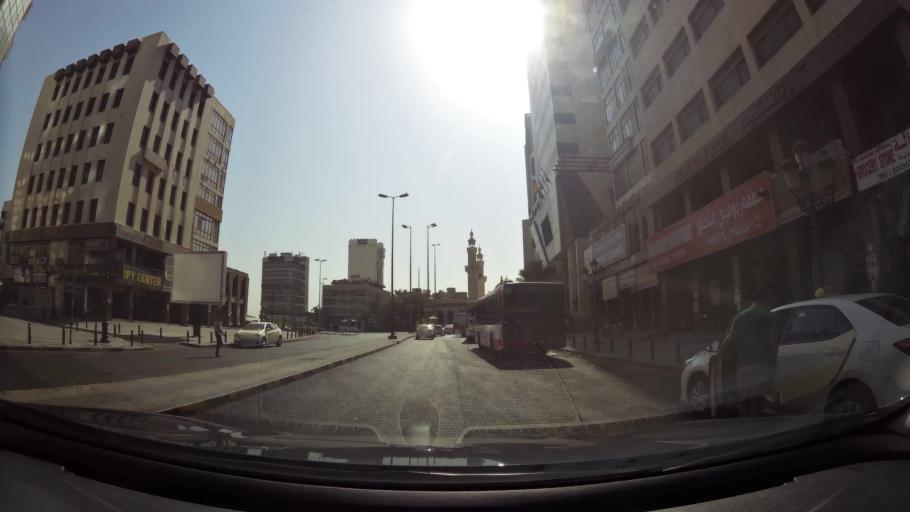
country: KW
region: Al Asimah
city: Kuwait City
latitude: 29.3704
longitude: 47.9782
